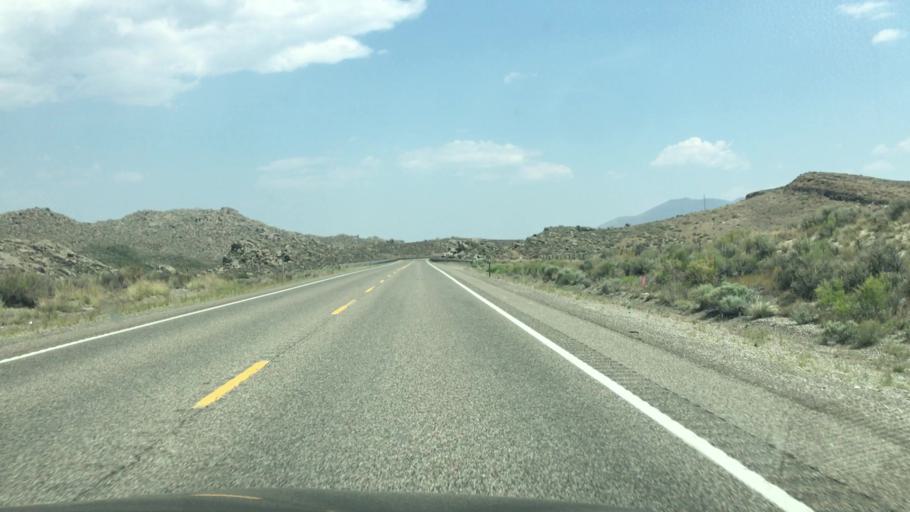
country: US
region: Nevada
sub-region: Elko County
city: Jackpot
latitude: 41.7334
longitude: -114.7901
